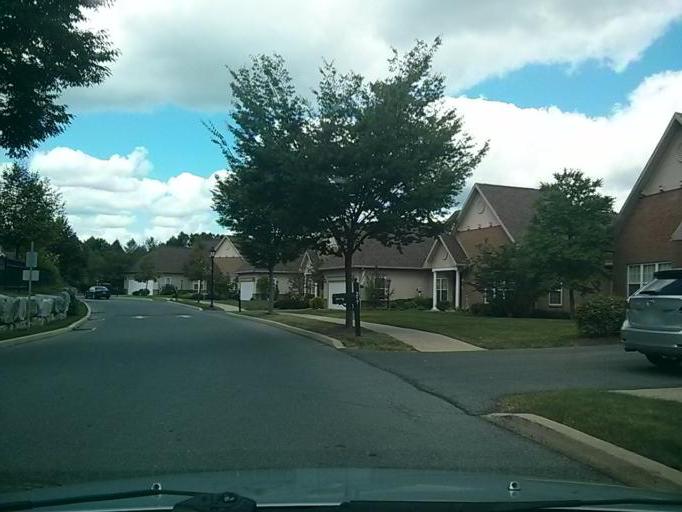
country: US
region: Pennsylvania
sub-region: Centre County
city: State College
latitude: 40.8246
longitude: -77.8717
